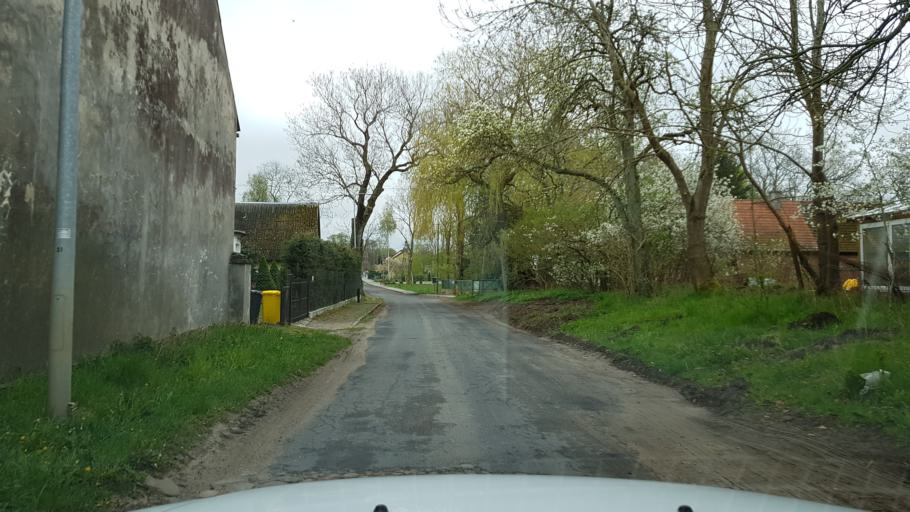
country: PL
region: West Pomeranian Voivodeship
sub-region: Powiat kolobrzeski
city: Ryman
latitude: 54.0308
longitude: 15.5258
